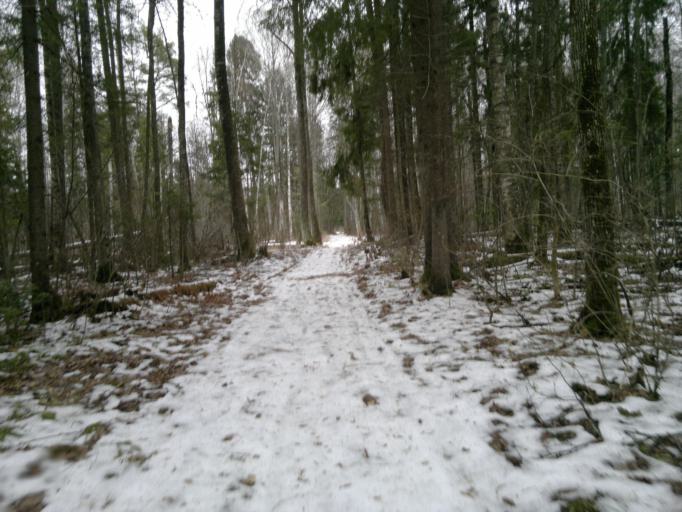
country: RU
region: Mariy-El
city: Yoshkar-Ola
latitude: 56.6085
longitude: 47.9580
